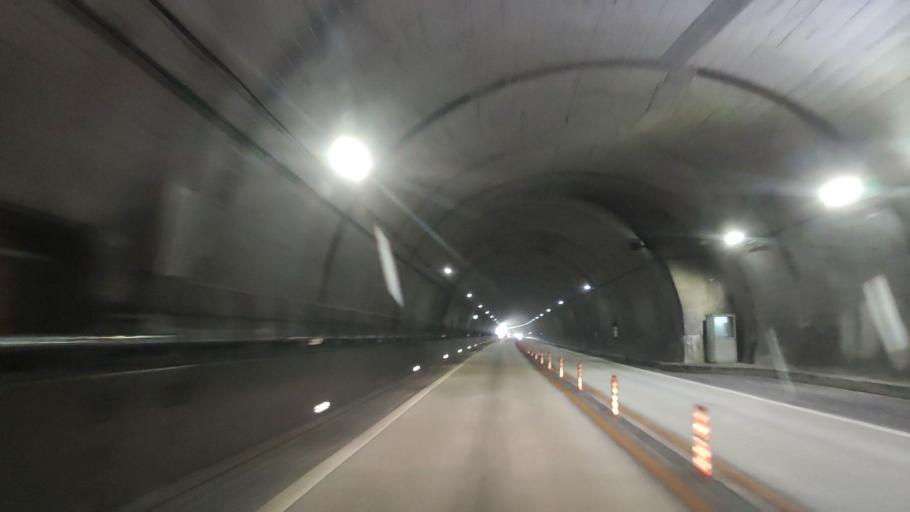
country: JP
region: Ehime
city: Hojo
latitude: 34.0839
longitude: 132.9775
